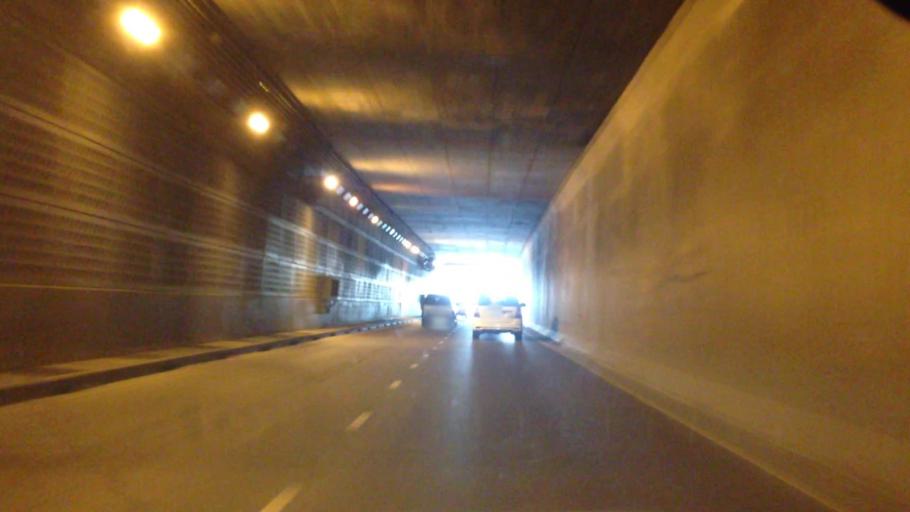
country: TH
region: Bangkok
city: Bang Na
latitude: 13.6778
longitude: 100.6461
